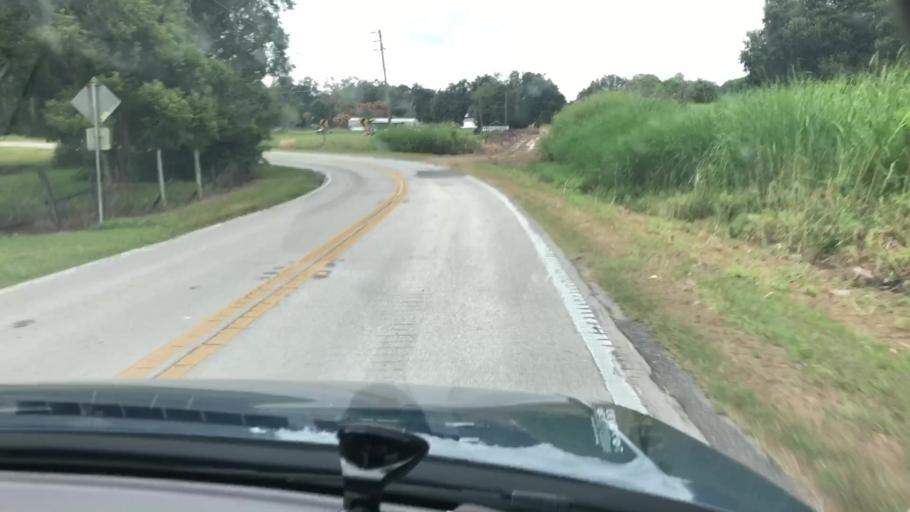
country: US
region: Florida
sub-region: Polk County
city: Kathleen
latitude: 28.1239
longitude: -82.0283
